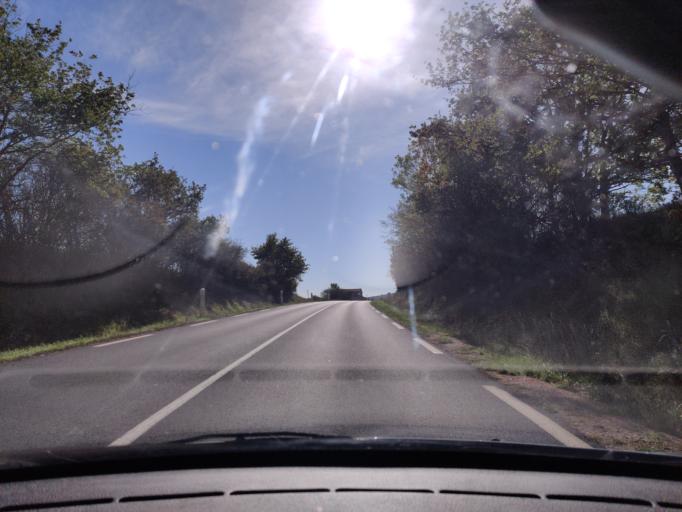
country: FR
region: Auvergne
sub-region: Departement du Puy-de-Dome
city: Combronde
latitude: 46.0033
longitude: 3.0939
